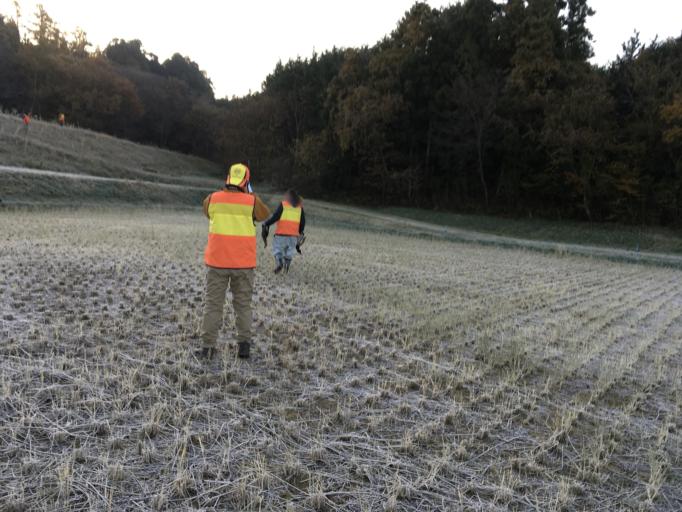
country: JP
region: Iwate
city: Ichinoseki
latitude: 38.7954
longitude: 141.1875
